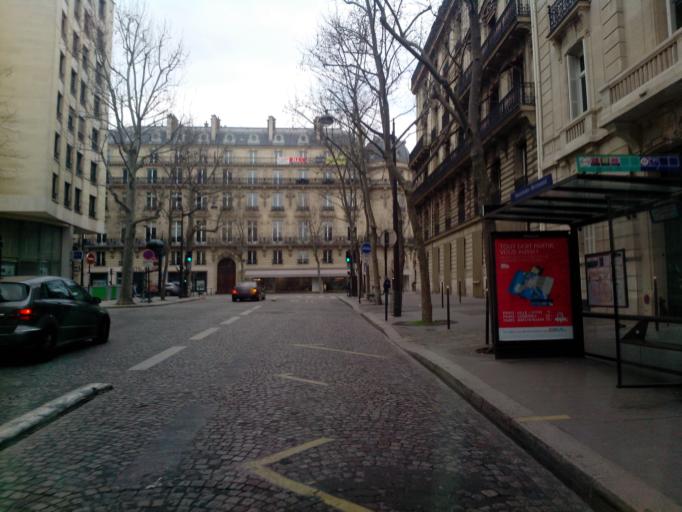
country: FR
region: Ile-de-France
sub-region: Departement des Hauts-de-Seine
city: Clichy
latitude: 48.8746
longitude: 2.3145
